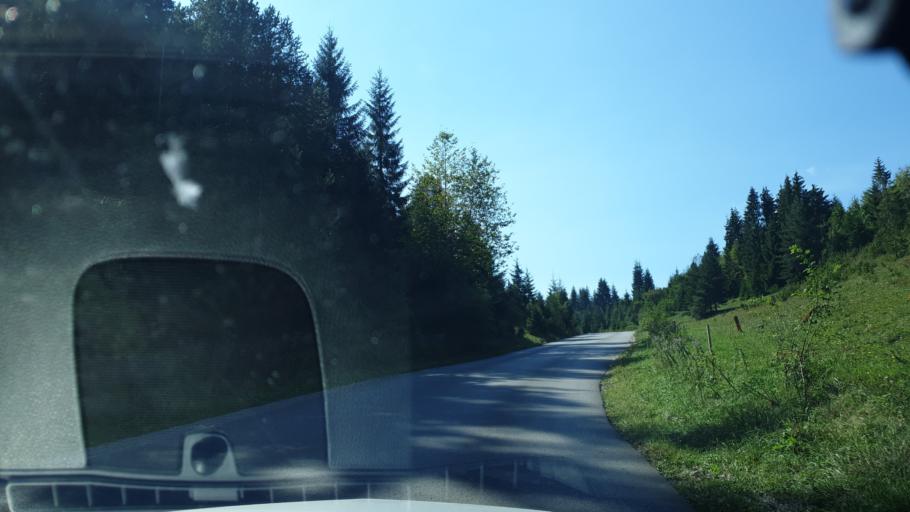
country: RS
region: Central Serbia
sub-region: Zlatiborski Okrug
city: Nova Varos
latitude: 43.4311
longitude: 19.8735
